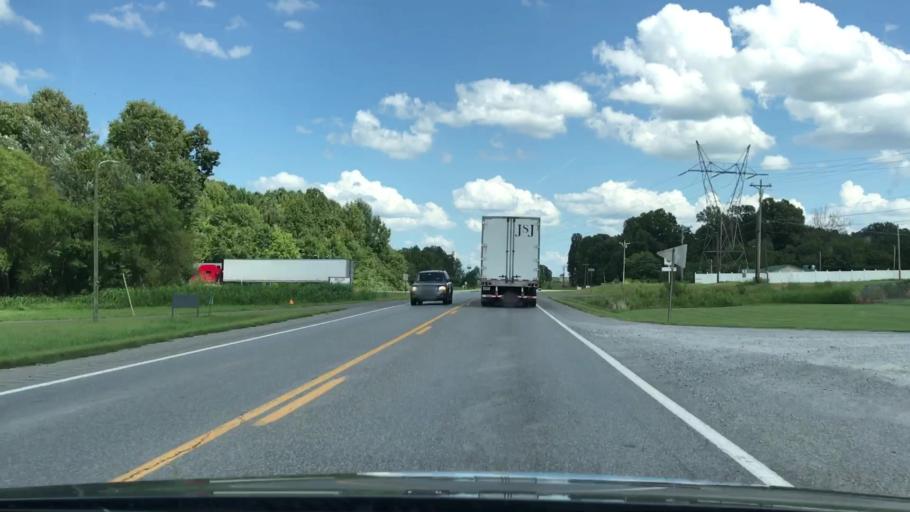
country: US
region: Kentucky
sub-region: Marshall County
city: Calvert City
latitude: 37.0035
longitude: -88.3385
